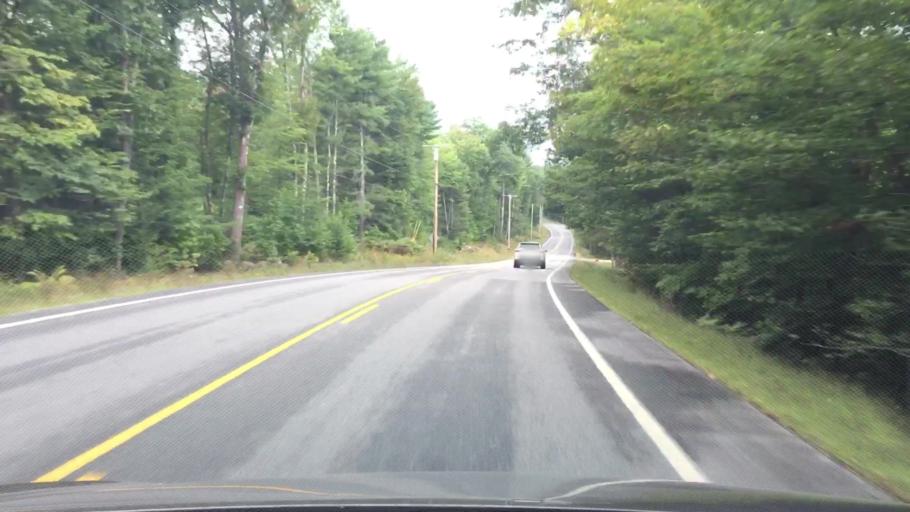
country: US
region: Maine
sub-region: Oxford County
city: Hartford
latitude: 44.3511
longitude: -70.3018
